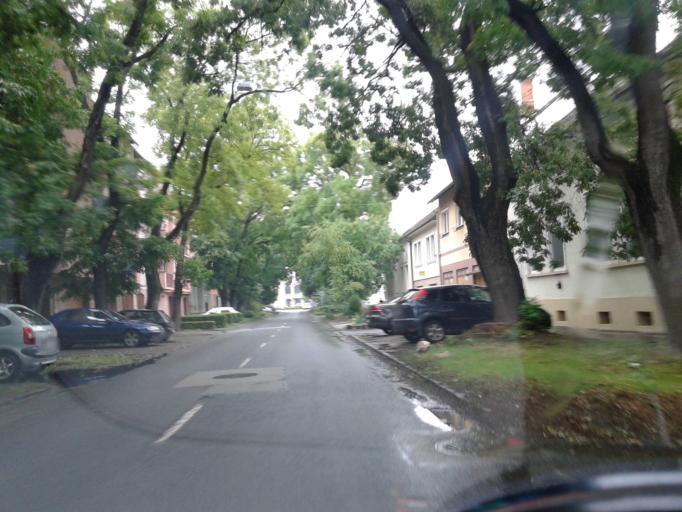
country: HU
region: Csongrad
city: Szeged
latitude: 46.2413
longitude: 20.1395
